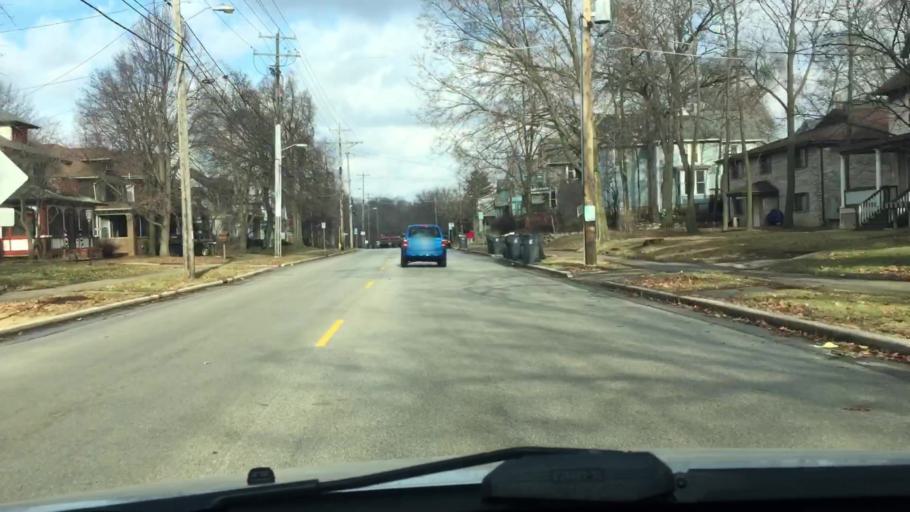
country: US
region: Wisconsin
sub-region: Waukesha County
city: Waukesha
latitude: 43.0076
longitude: -88.2366
